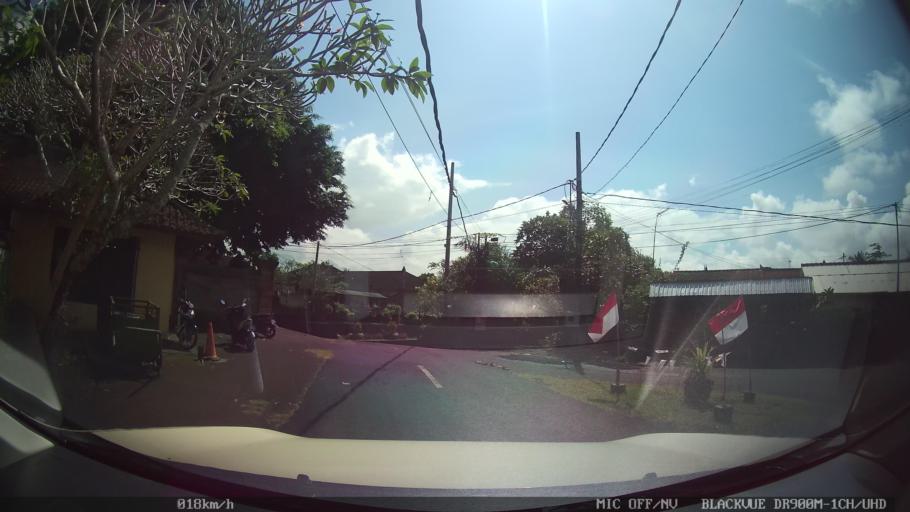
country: ID
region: Bali
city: Banjar Sedang
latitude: -8.5575
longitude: 115.2693
